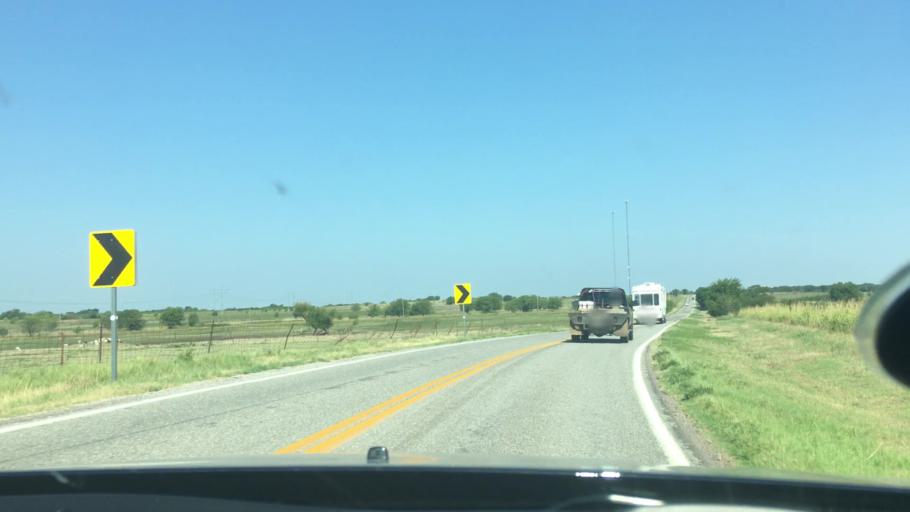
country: US
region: Oklahoma
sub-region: Johnston County
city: Tishomingo
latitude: 34.1873
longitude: -96.5269
